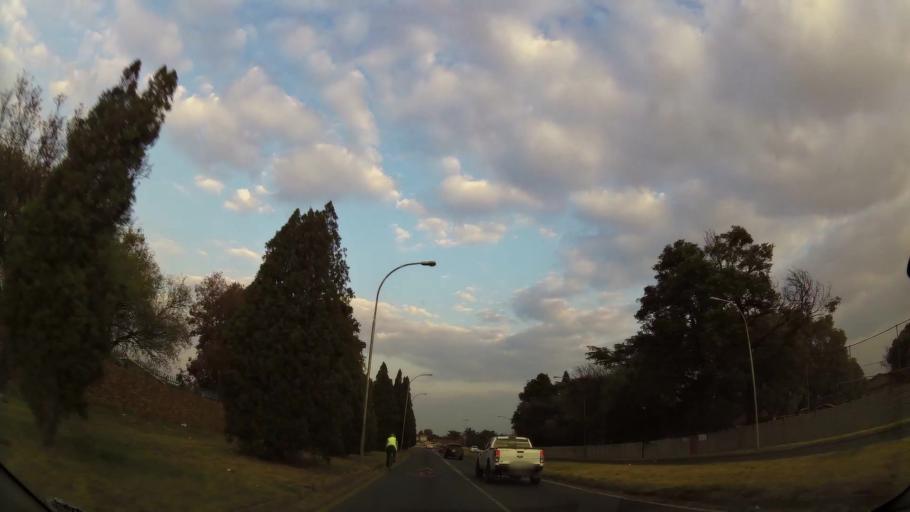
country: ZA
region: Gauteng
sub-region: Ekurhuleni Metropolitan Municipality
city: Benoni
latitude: -26.1685
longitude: 28.3105
